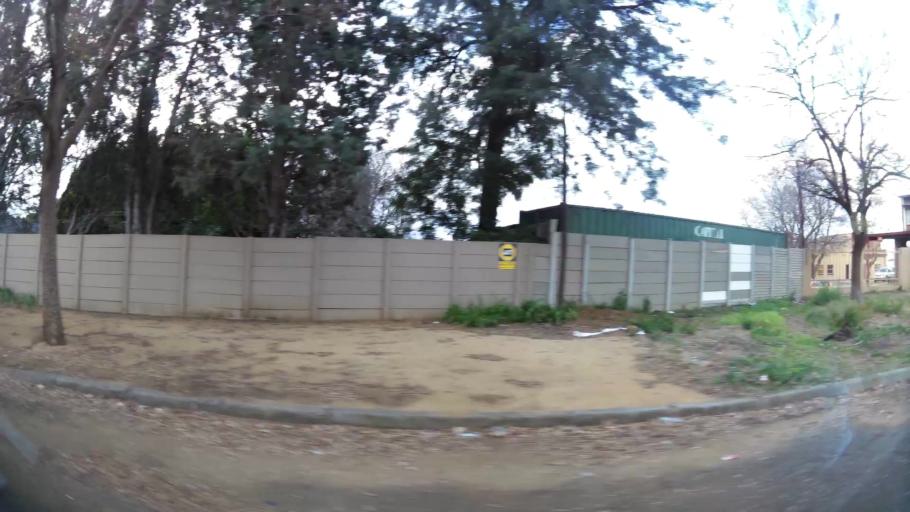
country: ZA
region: Orange Free State
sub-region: Lejweleputswa District Municipality
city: Welkom
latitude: -27.9790
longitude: 26.7304
